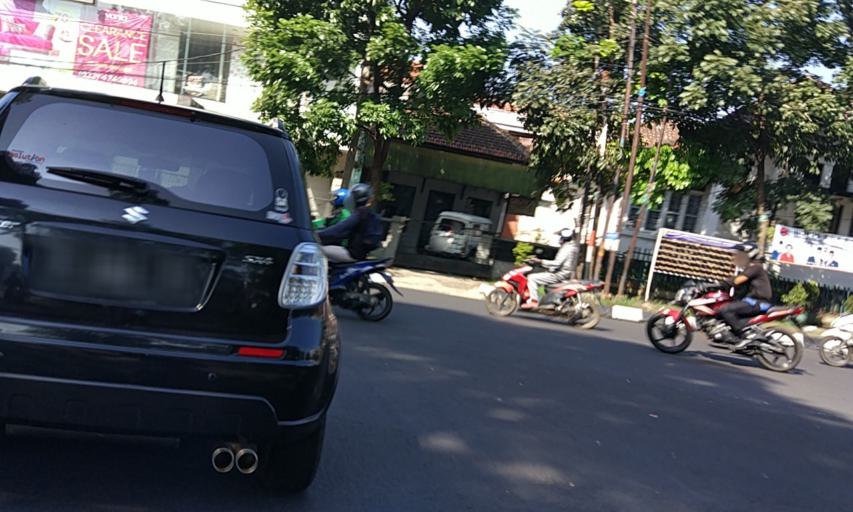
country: ID
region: West Java
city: Bandung
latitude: -6.9181
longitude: 107.6131
